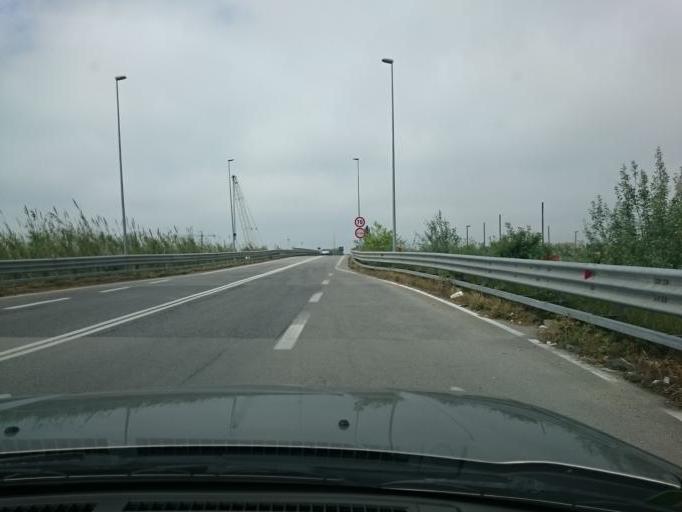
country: IT
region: Veneto
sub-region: Provincia di Venezia
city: Sant'Anna
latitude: 45.1896
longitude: 12.2766
